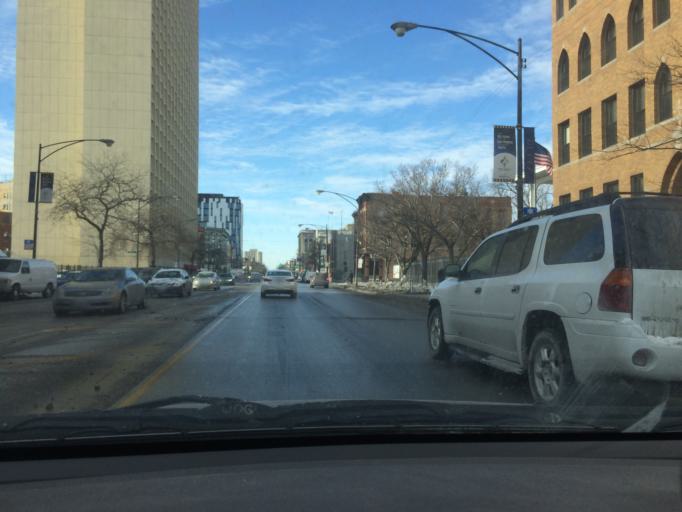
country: US
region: Illinois
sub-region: Cook County
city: Chicago
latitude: 41.9034
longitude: -87.6641
